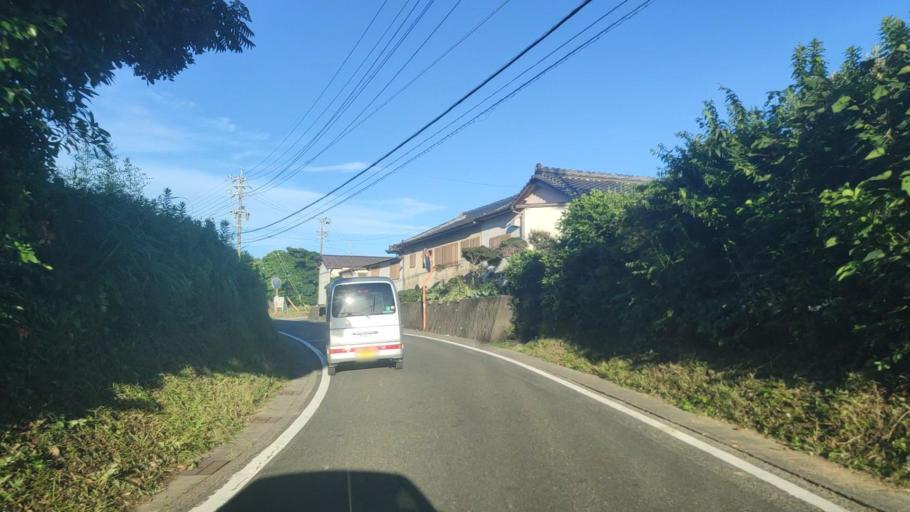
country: JP
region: Mie
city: Toba
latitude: 34.2552
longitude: 136.8259
